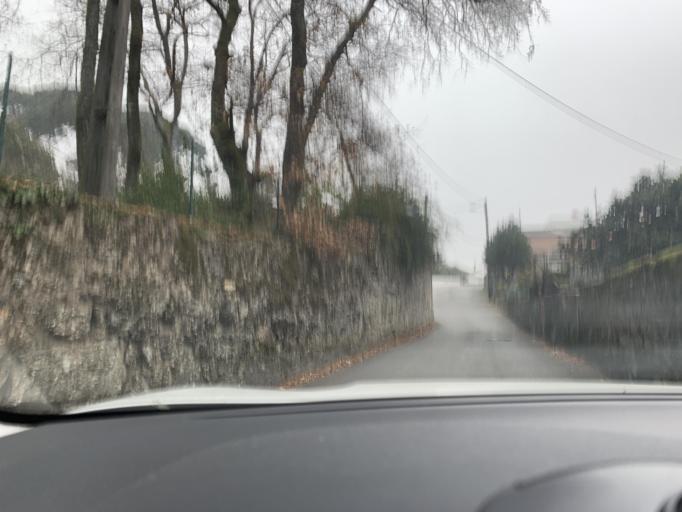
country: PT
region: Viseu
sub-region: Viseu
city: Viseu
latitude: 40.6572
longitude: -7.8973
